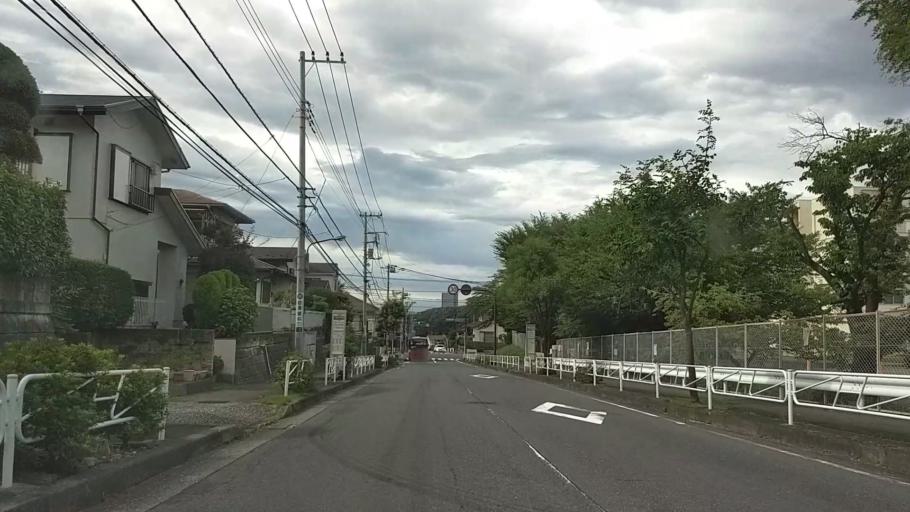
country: JP
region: Tokyo
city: Hachioji
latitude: 35.6305
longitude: 139.3457
